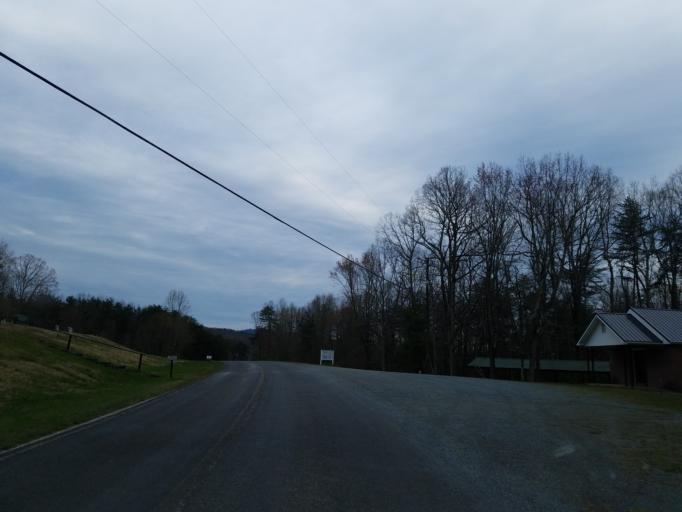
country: US
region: Georgia
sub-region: Fannin County
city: Blue Ridge
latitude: 34.7071
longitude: -84.2948
